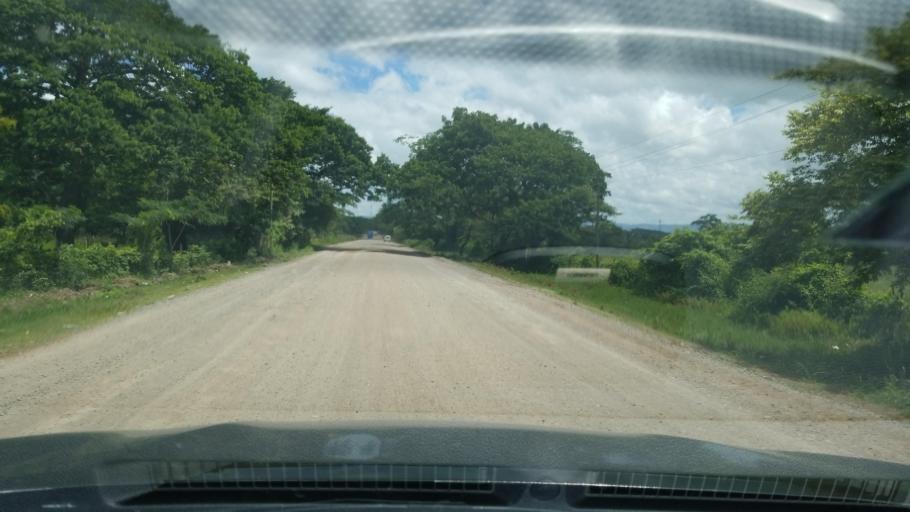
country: HN
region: Francisco Morazan
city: Talanga
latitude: 14.3915
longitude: -87.0763
